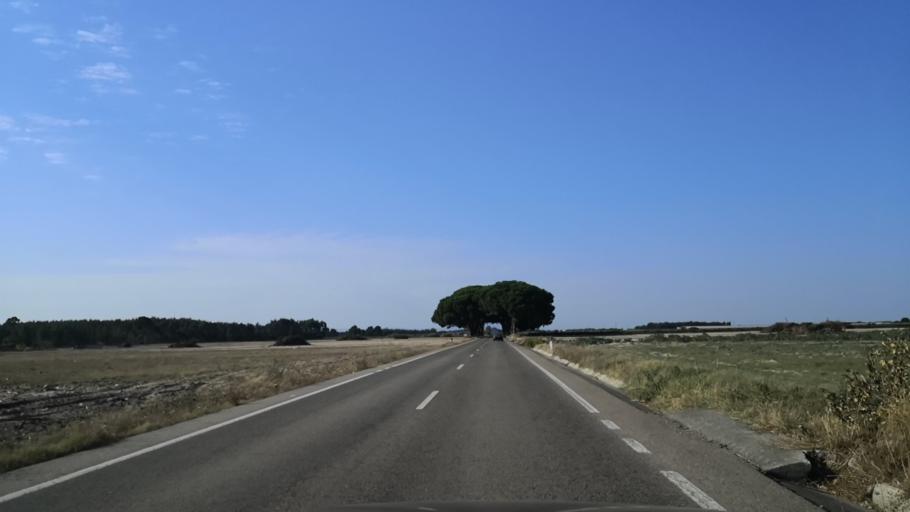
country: PT
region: Santarem
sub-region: Almeirim
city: Almeirim
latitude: 39.1590
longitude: -8.6204
